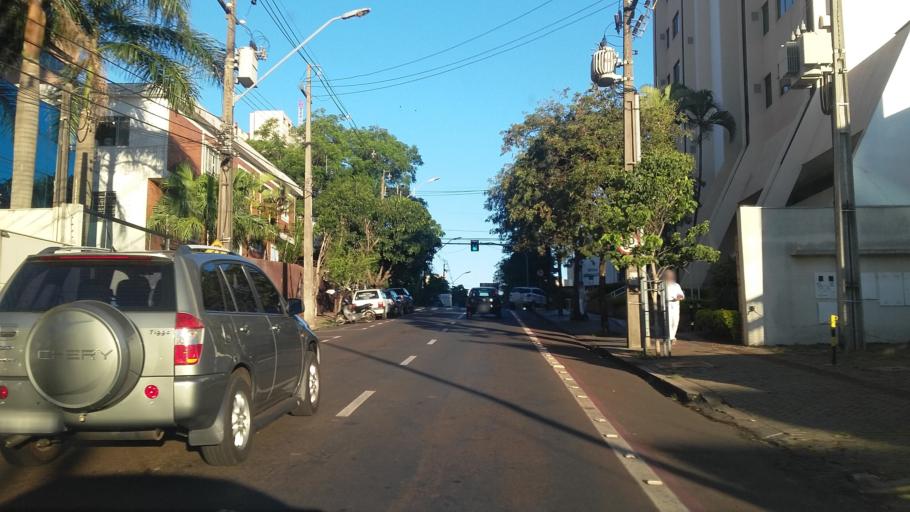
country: BR
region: Parana
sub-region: Londrina
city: Londrina
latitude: -23.3176
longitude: -51.1582
